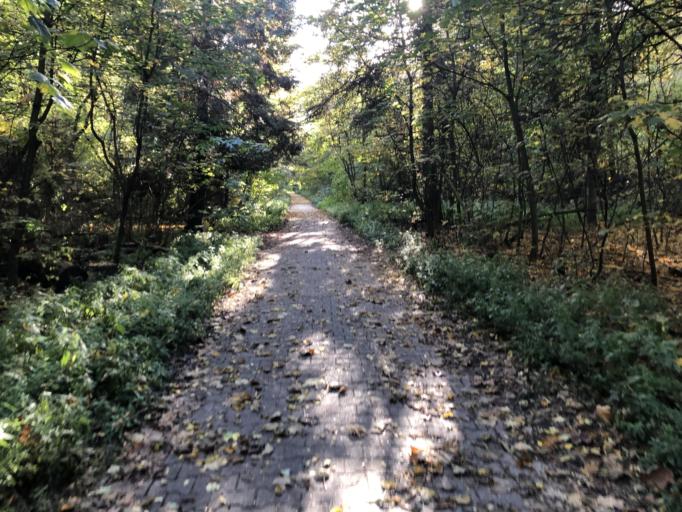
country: DE
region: Berlin
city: Grunewald
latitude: 52.4987
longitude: 13.2460
